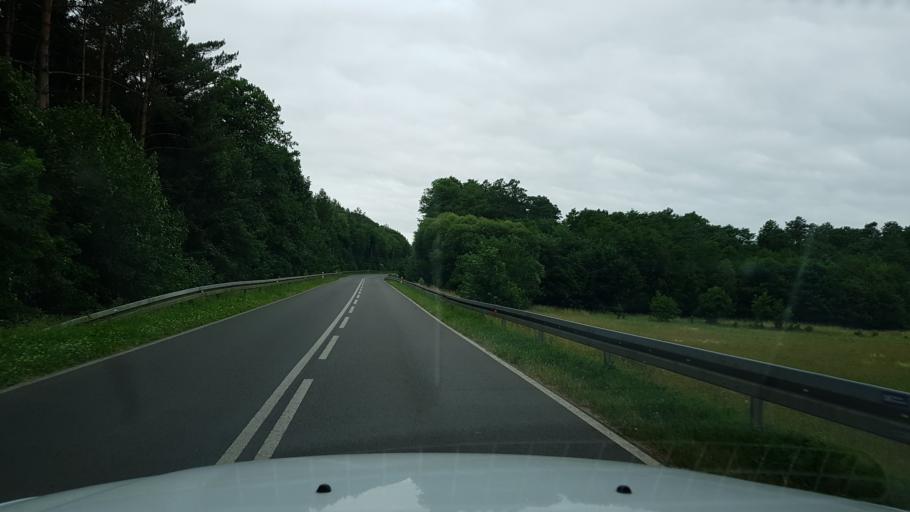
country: PL
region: West Pomeranian Voivodeship
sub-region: Powiat gryficki
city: Brojce
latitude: 53.9552
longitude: 15.3760
